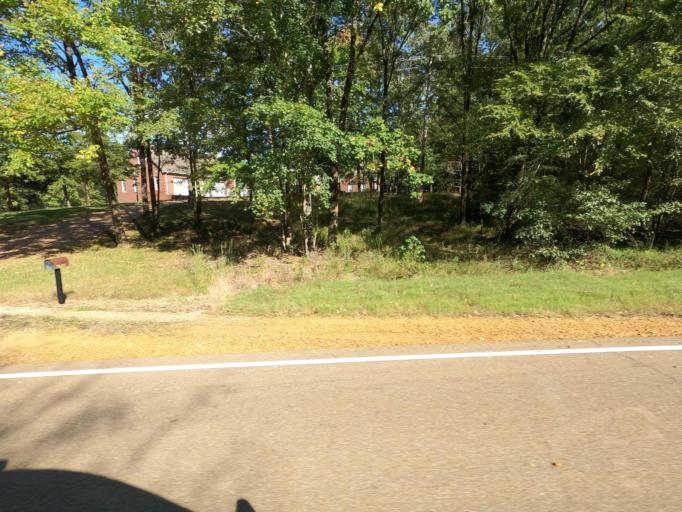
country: US
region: Tennessee
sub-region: Shelby County
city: Arlington
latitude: 35.2484
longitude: -89.6501
